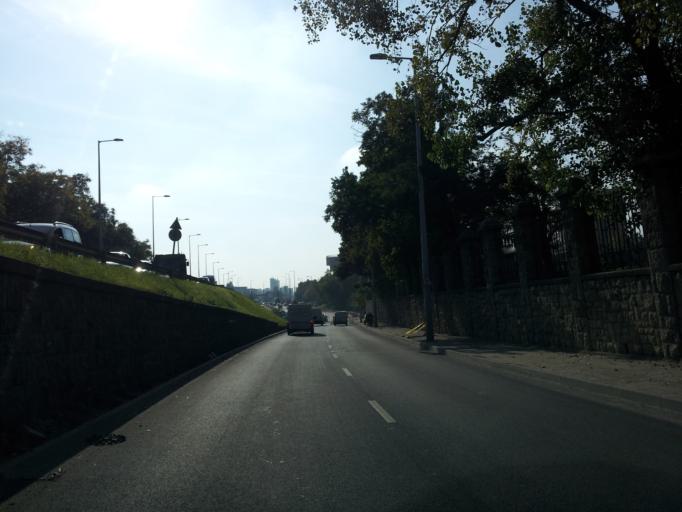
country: HU
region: Budapest
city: Budapest XI. keruelet
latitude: 47.4756
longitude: 19.0239
